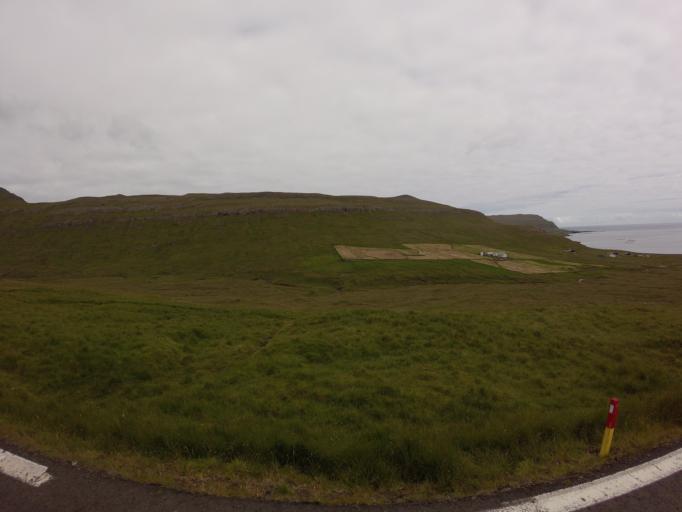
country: FO
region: Suduroy
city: Tvoroyri
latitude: 61.5342
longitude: -6.8336
